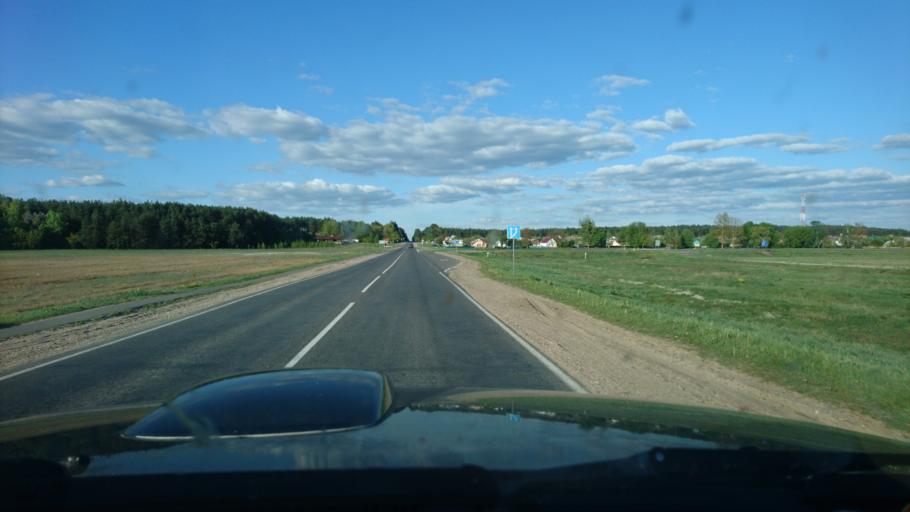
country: BY
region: Brest
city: Ivatsevichy
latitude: 52.7234
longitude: 25.3665
